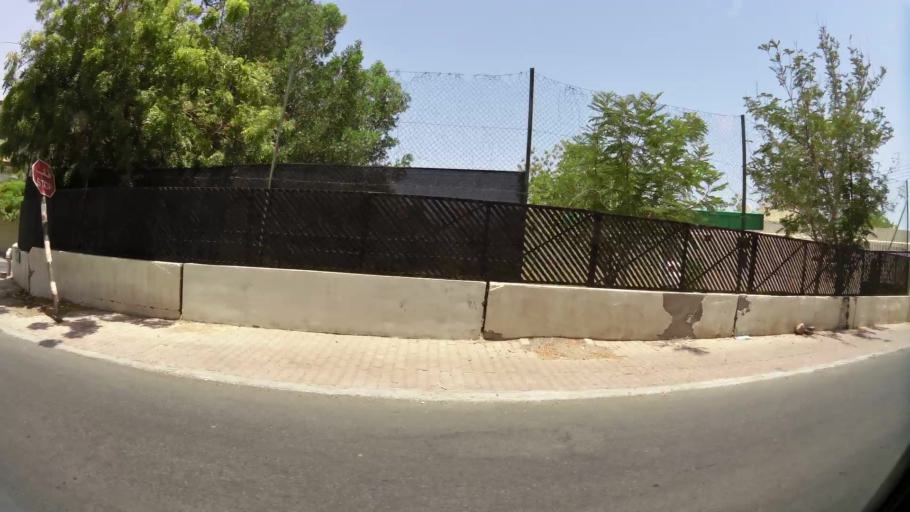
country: OM
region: Muhafazat Masqat
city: Bawshar
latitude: 23.5997
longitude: 58.4579
